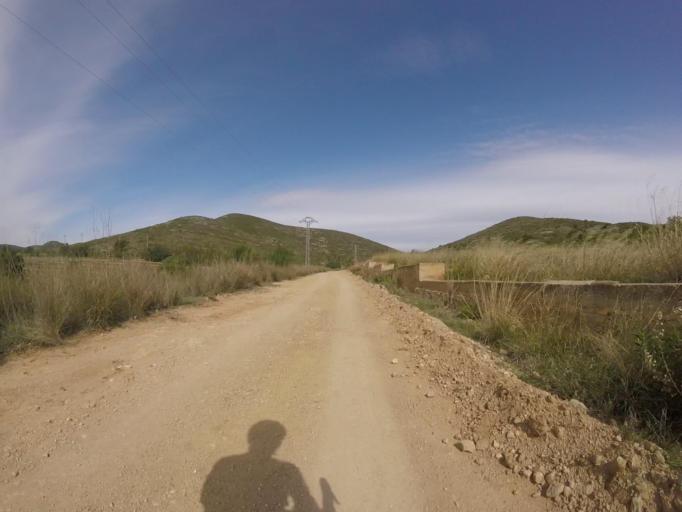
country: ES
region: Valencia
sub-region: Provincia de Castello
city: Torreblanca
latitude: 40.1964
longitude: 0.1585
